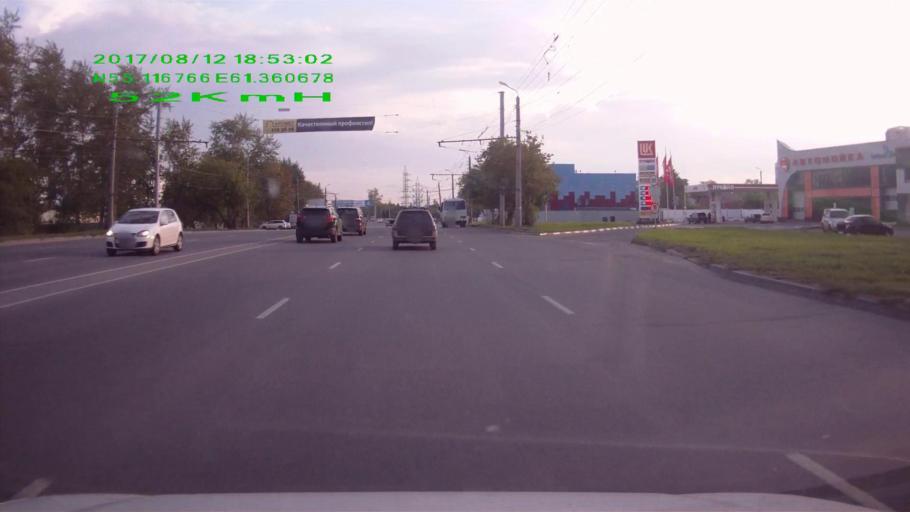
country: RU
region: Chelyabinsk
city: Novosineglazovskiy
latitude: 55.1126
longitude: 61.3574
